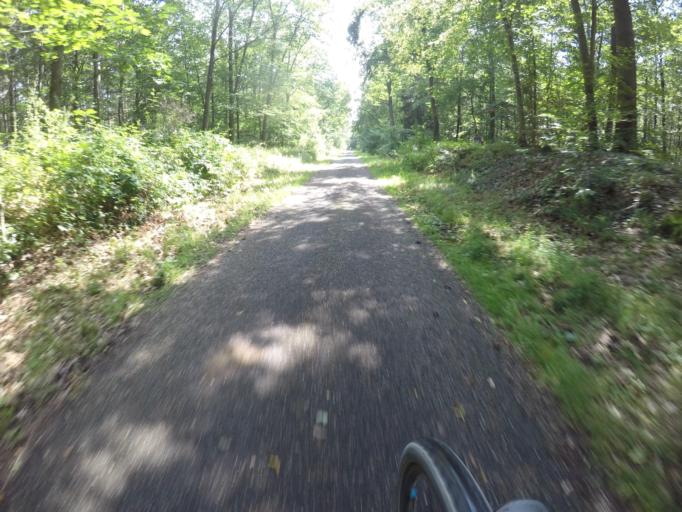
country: DE
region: Baden-Wuerttemberg
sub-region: Karlsruhe Region
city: Hambrucken
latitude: 49.2177
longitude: 8.5721
